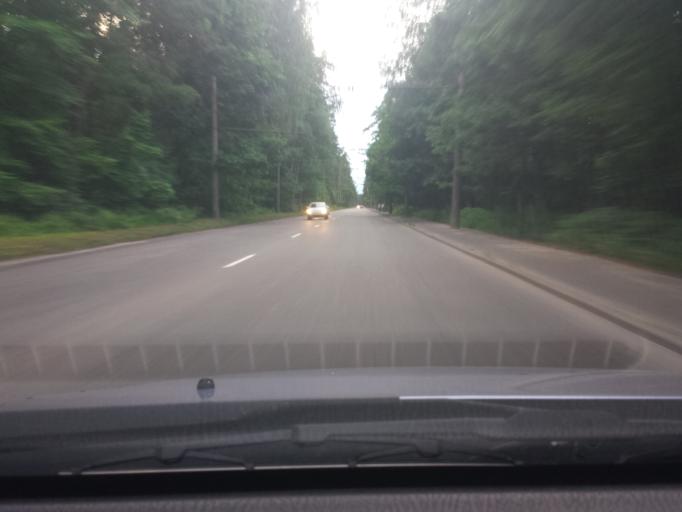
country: LV
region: Stopini
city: Ulbroka
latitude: 56.9609
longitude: 24.2252
